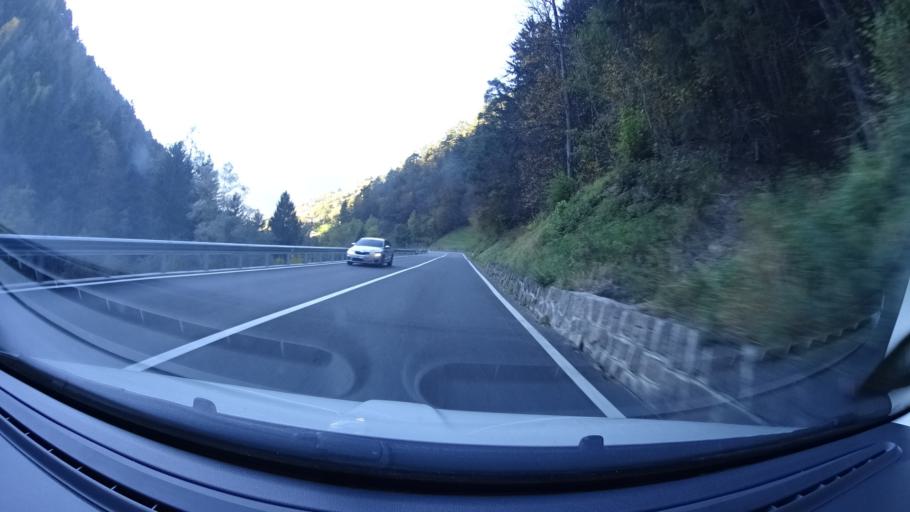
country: IT
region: Trentino-Alto Adige
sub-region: Bolzano
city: Laion
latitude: 46.5955
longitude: 11.5711
